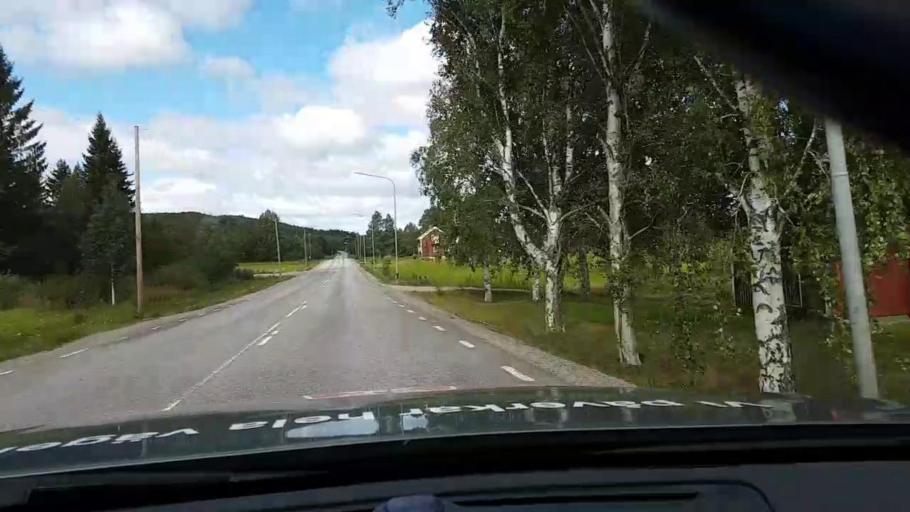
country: SE
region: Vaesternorrland
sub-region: OErnskoeldsviks Kommun
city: Bredbyn
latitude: 63.4807
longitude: 18.0913
